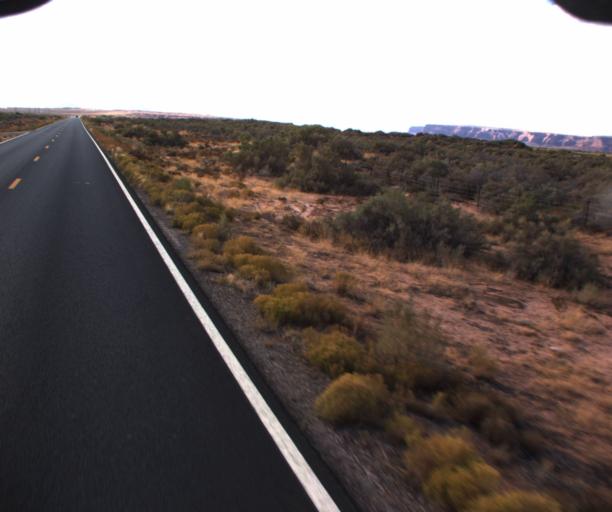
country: US
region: Arizona
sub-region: Apache County
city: Many Farms
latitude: 36.6353
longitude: -109.5867
